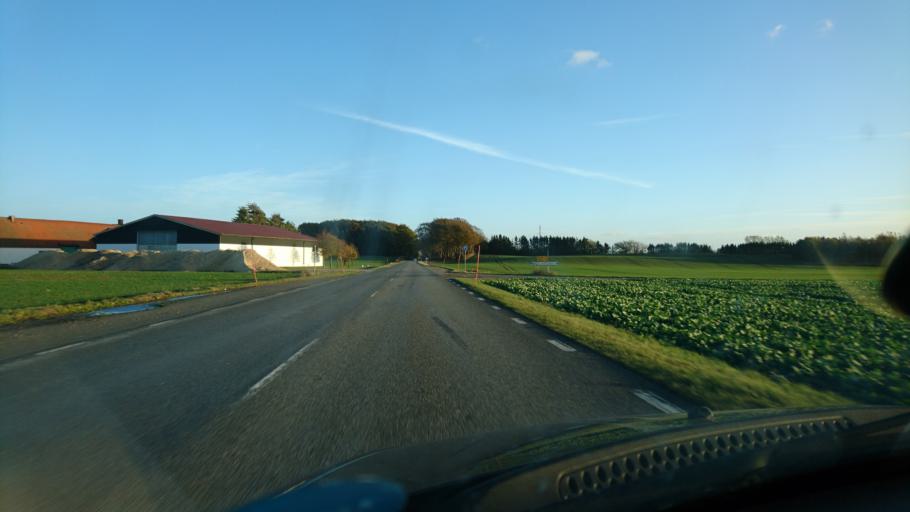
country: SE
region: Skane
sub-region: Simrishamns Kommun
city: Simrishamn
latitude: 55.4684
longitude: 14.1806
